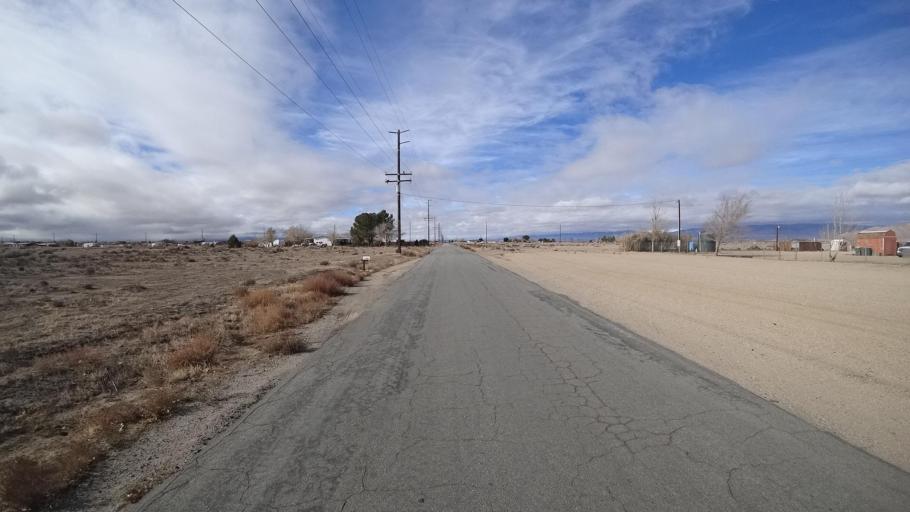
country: US
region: California
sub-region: Kern County
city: Rosamond
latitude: 34.8346
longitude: -118.2515
